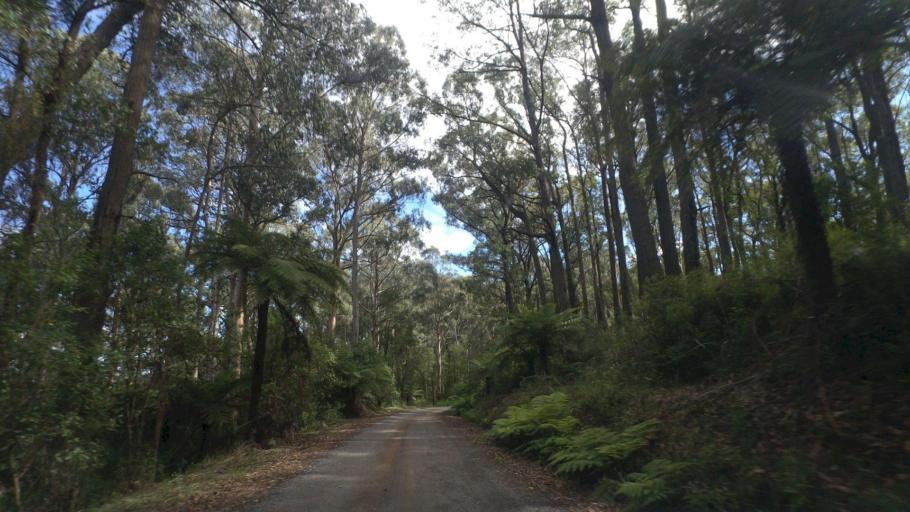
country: AU
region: Victoria
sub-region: Cardinia
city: Gembrook
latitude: -37.9196
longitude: 145.6115
